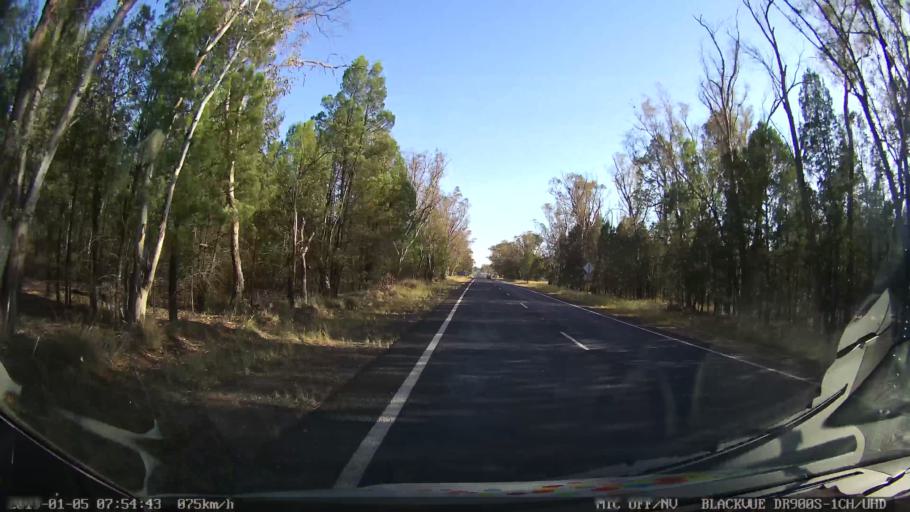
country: AU
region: New South Wales
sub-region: Gilgandra
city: Gilgandra
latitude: -31.7305
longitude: 148.6508
